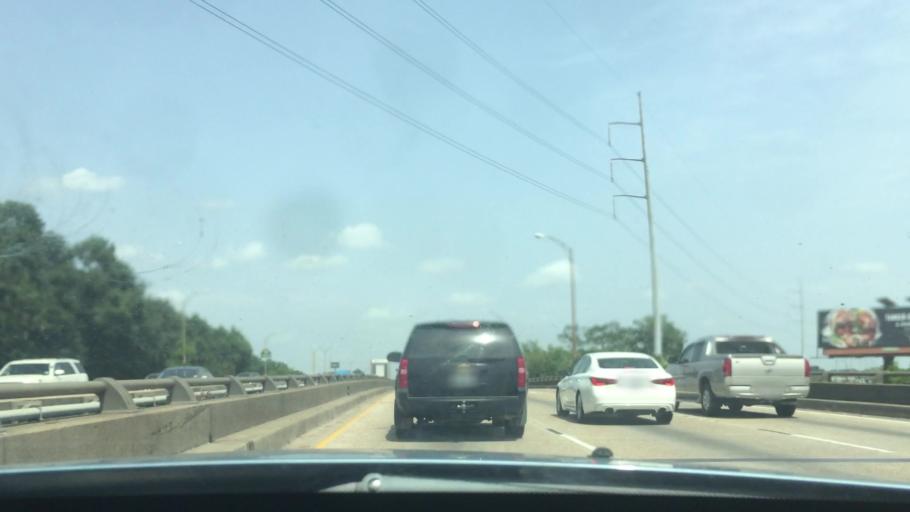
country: US
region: Louisiana
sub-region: East Baton Rouge Parish
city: Baton Rouge
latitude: 30.4245
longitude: -91.1558
